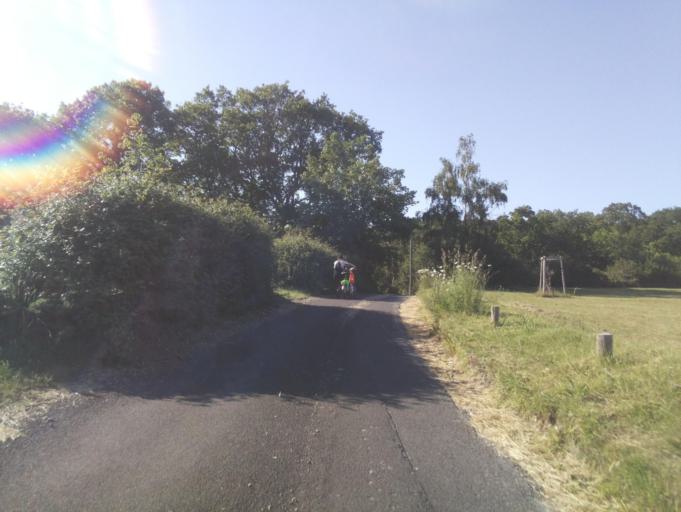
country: GB
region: England
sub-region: Hampshire
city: Compton
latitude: 50.9991
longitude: -1.3534
